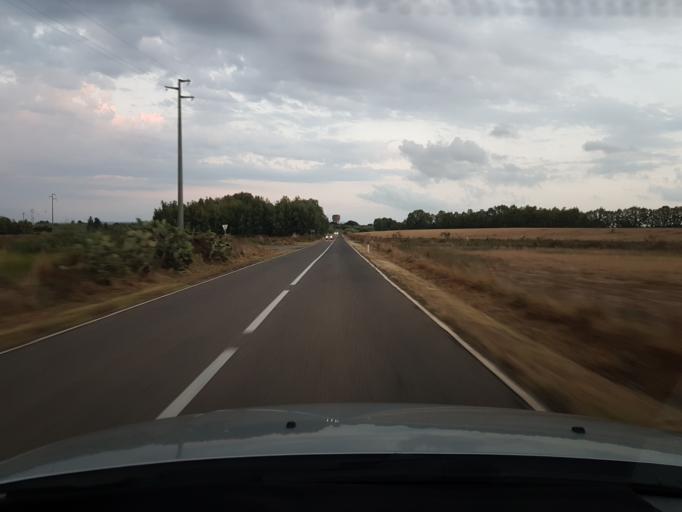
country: IT
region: Sardinia
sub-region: Provincia di Oristano
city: Tramatza
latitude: 40.0135
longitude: 8.6449
